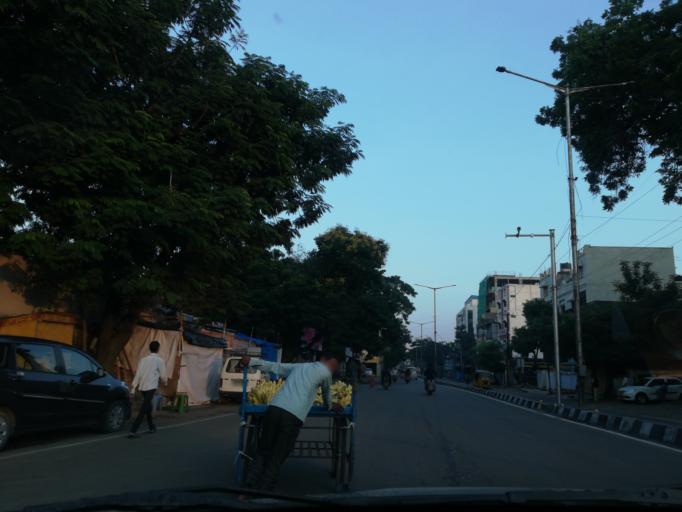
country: IN
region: Telangana
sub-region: Rangareddi
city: Gaddi Annaram
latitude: 17.3946
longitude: 78.4986
